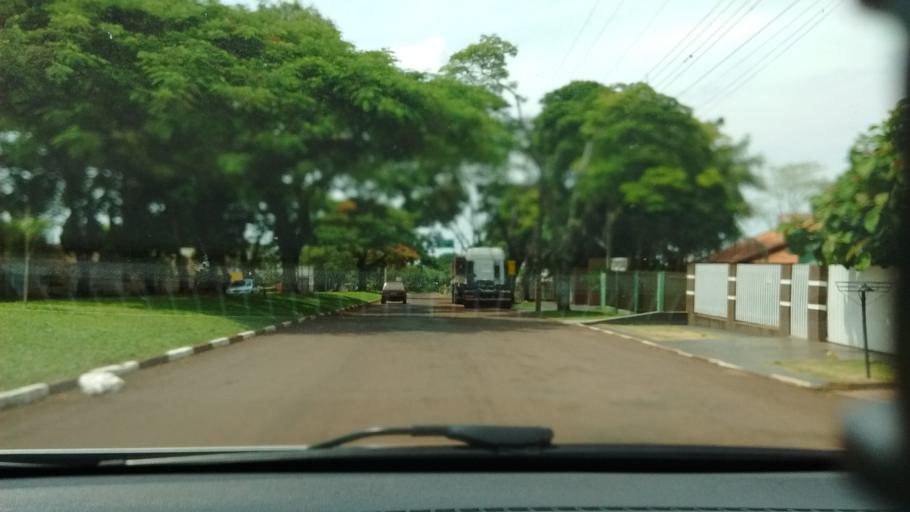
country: BR
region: Parana
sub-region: Corbelia
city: Corbelia
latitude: -24.5432
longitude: -52.9822
